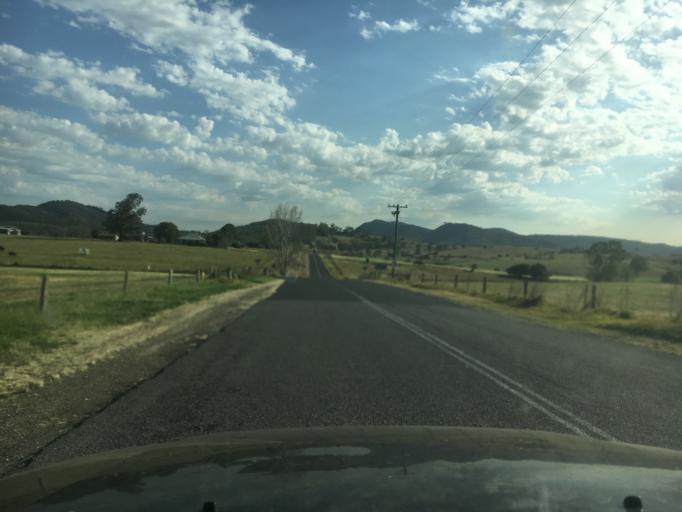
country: AU
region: New South Wales
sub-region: Cessnock
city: Branxton
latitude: -32.6070
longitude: 151.3481
